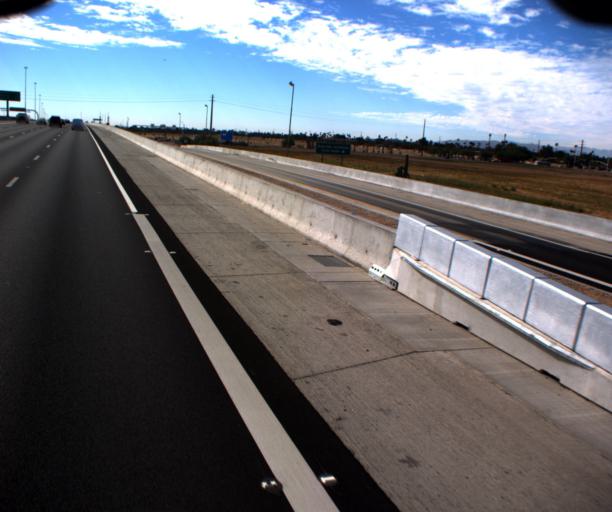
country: US
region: Arizona
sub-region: Maricopa County
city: Scottsdale
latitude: 33.4978
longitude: -111.8881
